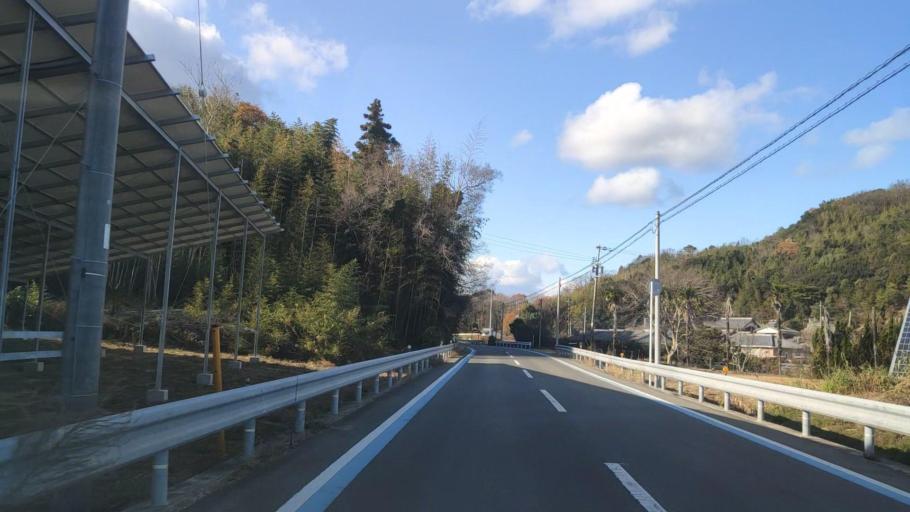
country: JP
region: Hiroshima
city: Innoshima
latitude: 34.2297
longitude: 133.1065
